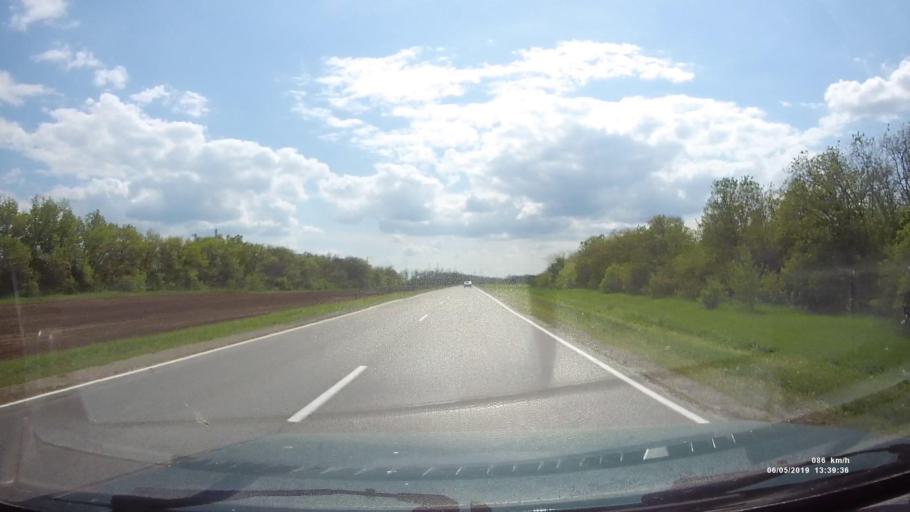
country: RU
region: Rostov
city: Ust'-Donetskiy
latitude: 47.6737
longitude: 40.7014
